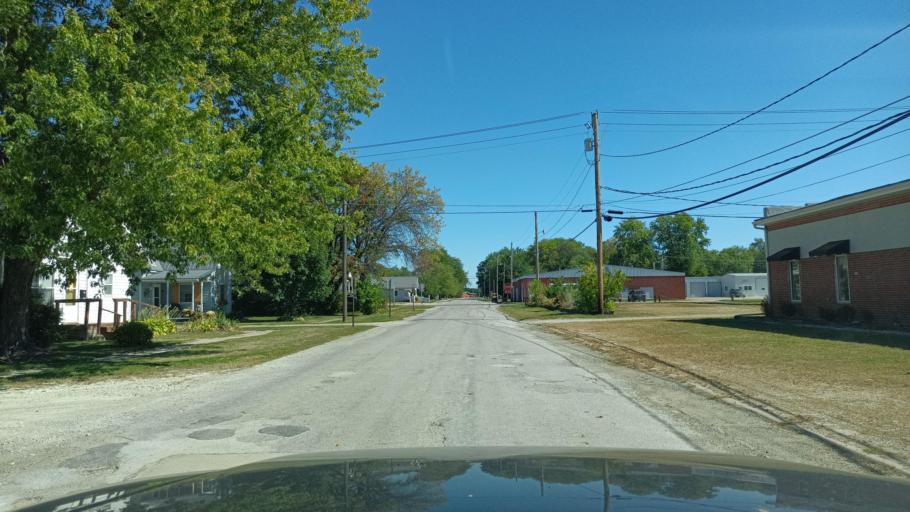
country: US
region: Missouri
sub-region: Macon County
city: La Plata
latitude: 40.0234
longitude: -92.4897
